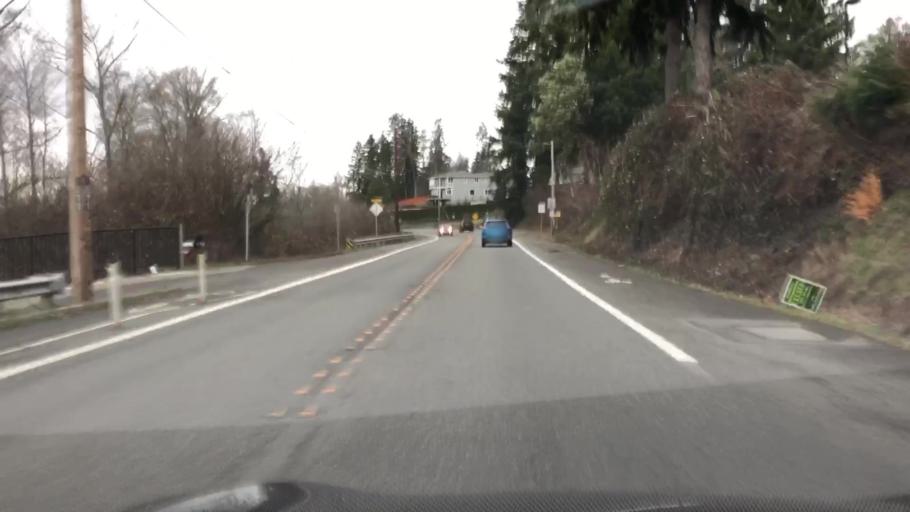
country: US
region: Washington
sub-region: King County
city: Sammamish
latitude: 47.6541
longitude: -122.0912
